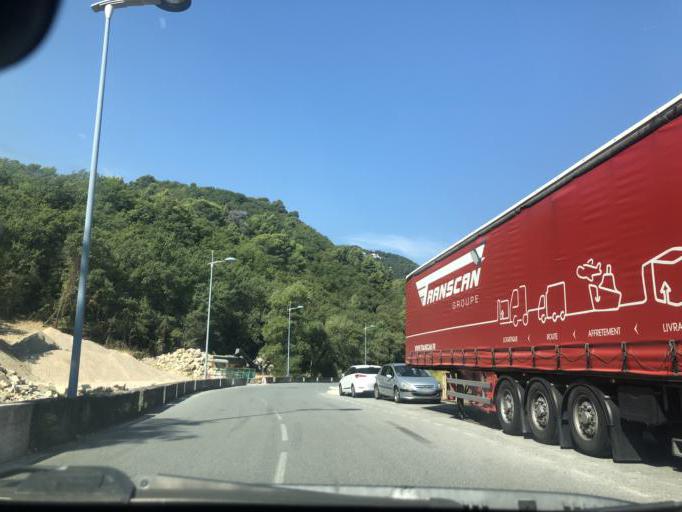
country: FR
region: Provence-Alpes-Cote d'Azur
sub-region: Departement des Alpes-Maritimes
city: Saint-Martin-du-Var
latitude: 43.8076
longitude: 7.1846
